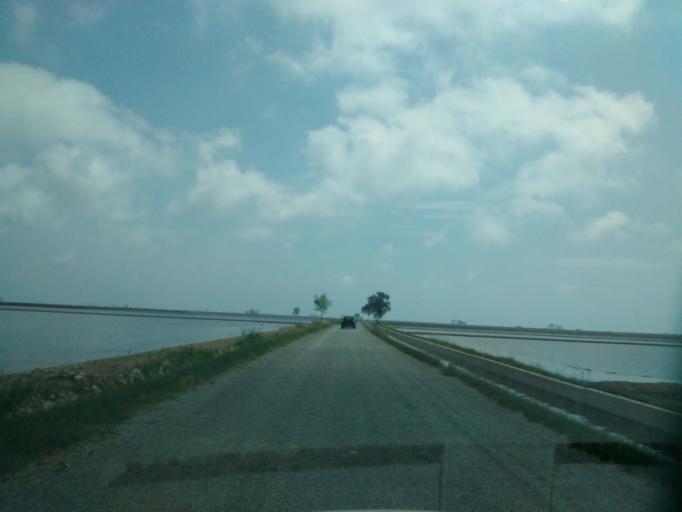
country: ES
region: Catalonia
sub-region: Provincia de Tarragona
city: Deltebre
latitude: 40.6889
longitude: 0.7817
